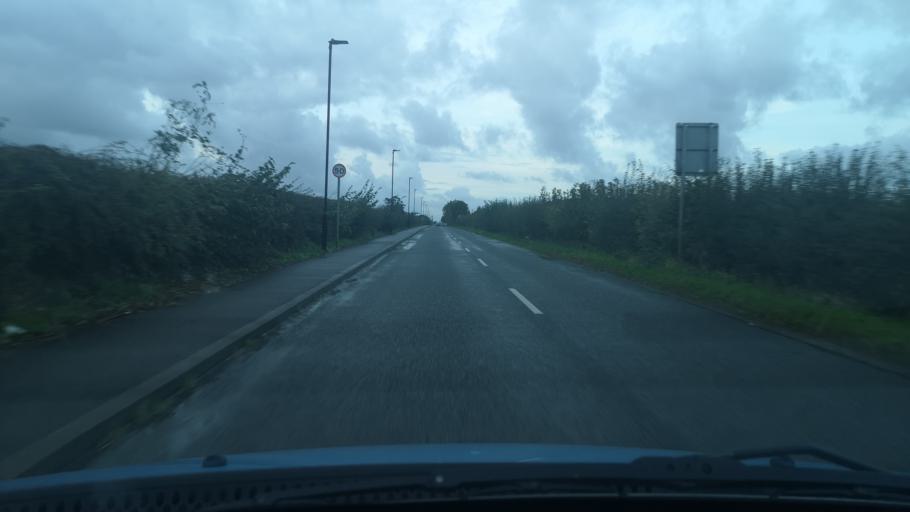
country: GB
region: England
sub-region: Doncaster
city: Norton
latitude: 53.6276
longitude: -1.1827
